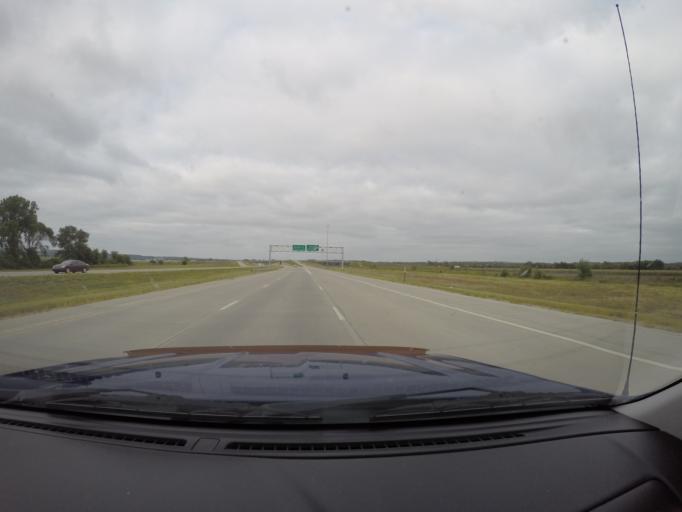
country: US
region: Kansas
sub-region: Riley County
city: Ogden
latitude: 39.1266
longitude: -96.6792
